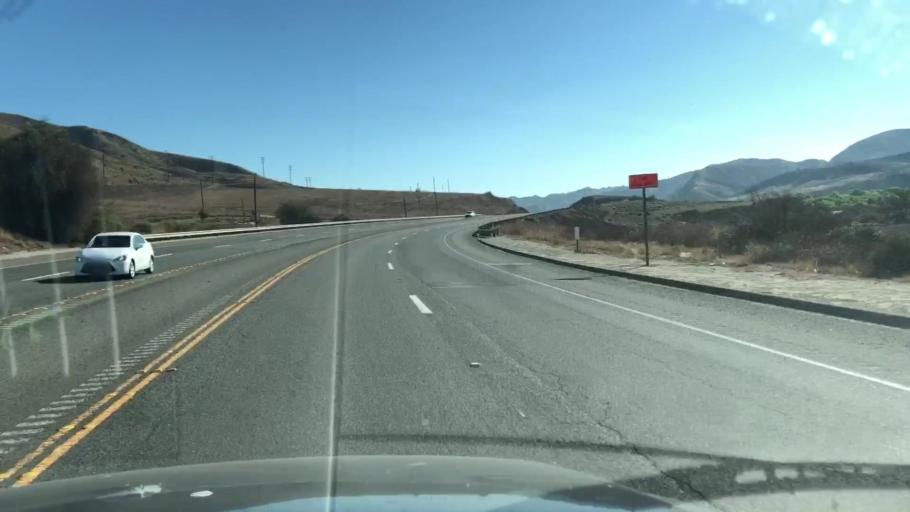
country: US
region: California
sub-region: Los Angeles County
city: Val Verde
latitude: 34.4076
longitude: -118.6844
